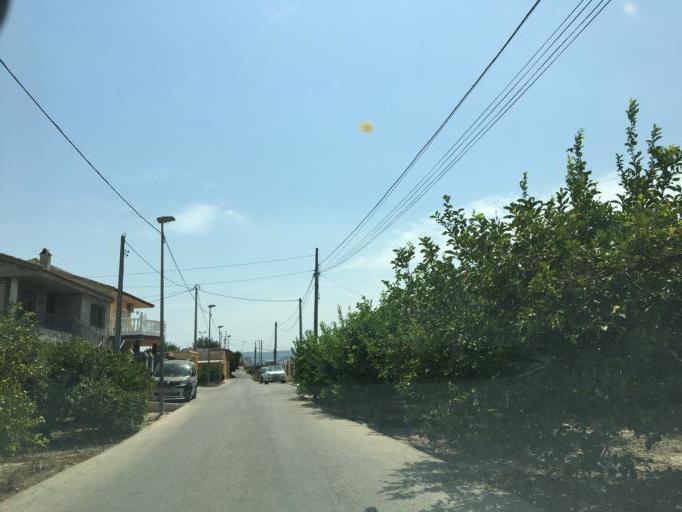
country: ES
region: Murcia
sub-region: Murcia
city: Santomera
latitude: 38.0240
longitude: -1.0467
